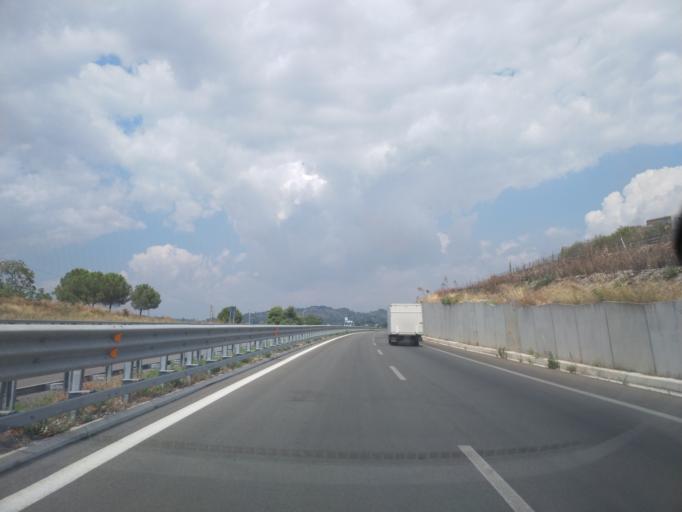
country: IT
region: Sicily
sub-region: Agrigento
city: Grotte
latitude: 37.3680
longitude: 13.7061
